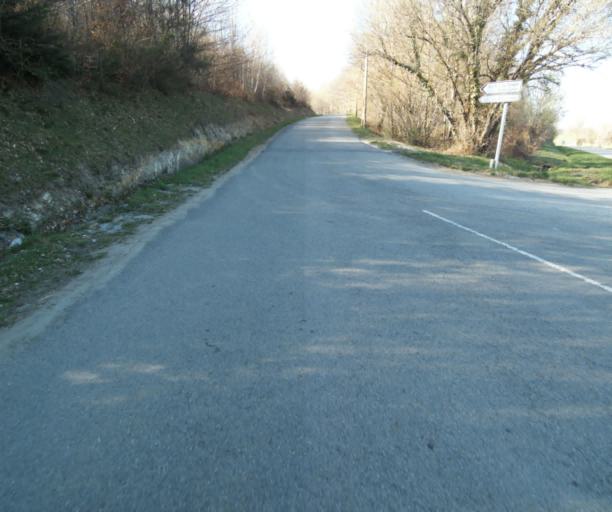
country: FR
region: Limousin
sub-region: Departement de la Correze
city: Seilhac
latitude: 45.3836
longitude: 1.7215
